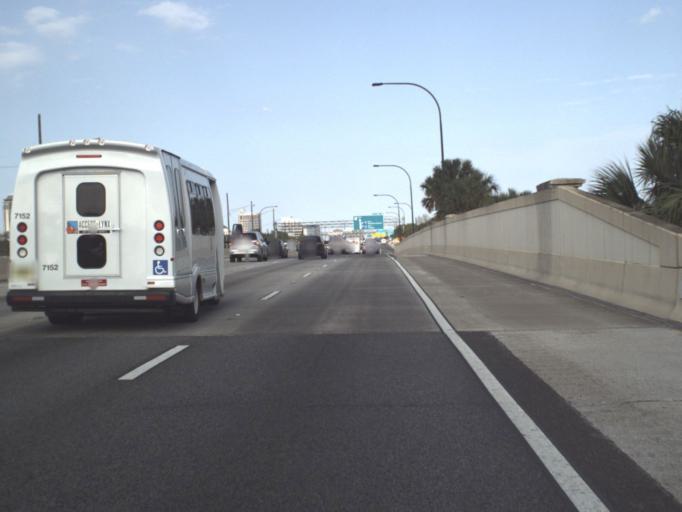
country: US
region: Florida
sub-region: Orange County
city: Orlando
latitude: 28.5351
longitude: -81.3976
